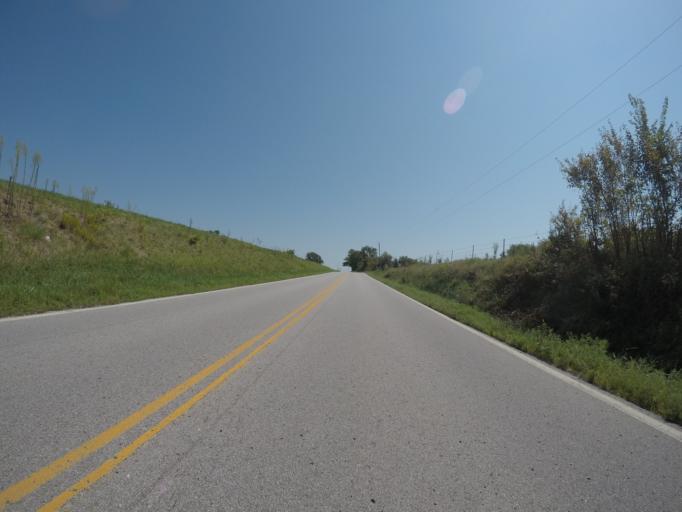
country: US
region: Kansas
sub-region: Leavenworth County
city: Lansing
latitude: 39.2356
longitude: -94.8648
